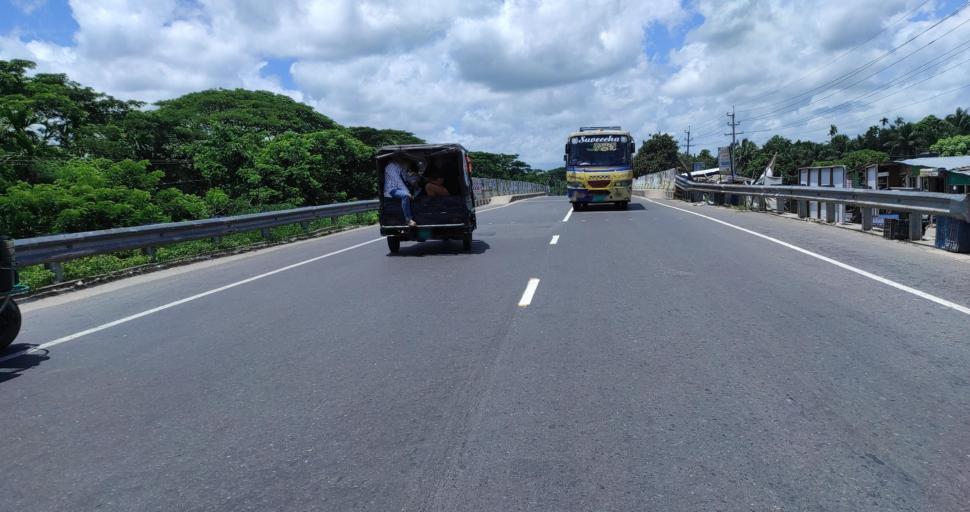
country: BD
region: Barisal
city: Barisal
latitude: 22.7903
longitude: 90.3000
